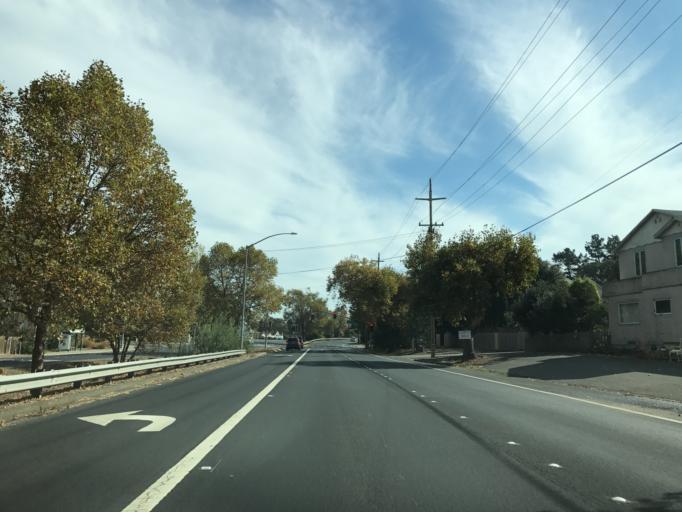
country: US
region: California
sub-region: Sonoma County
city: Petaluma
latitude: 38.2558
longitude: -122.6528
